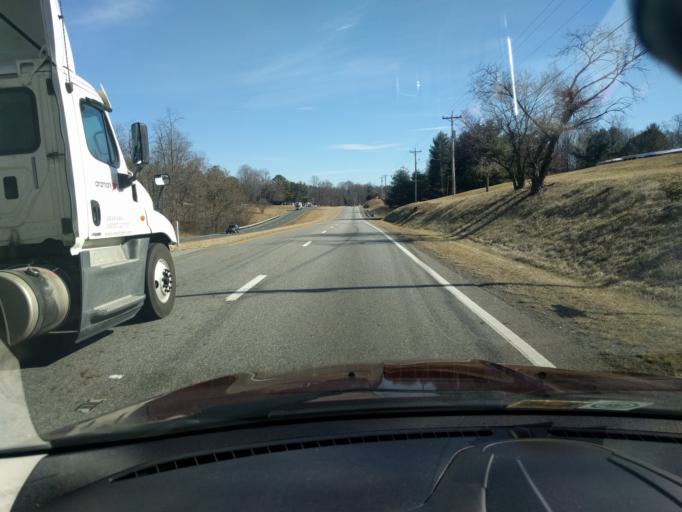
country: US
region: Virginia
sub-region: City of Bedford
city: Bedford
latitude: 37.3563
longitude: -79.6614
